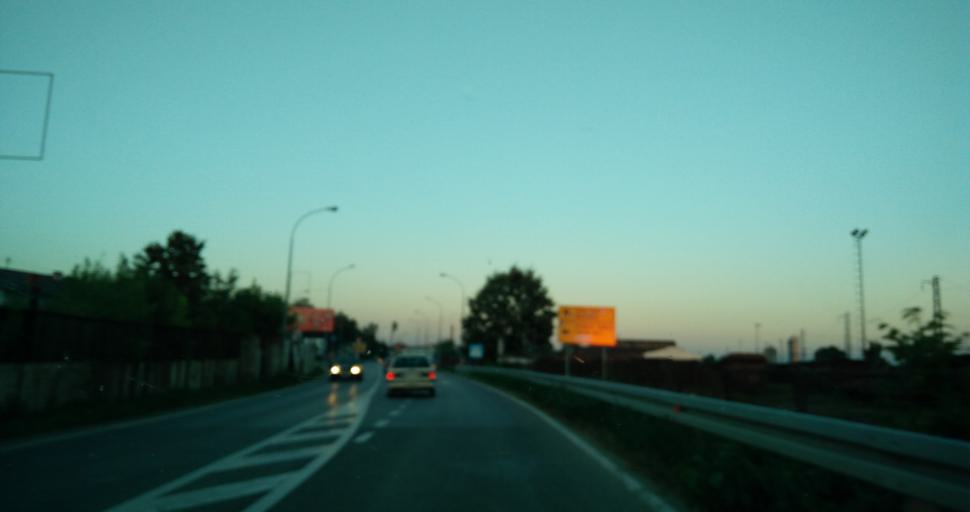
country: BA
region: Republika Srpska
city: Prijedor
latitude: 44.9802
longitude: 16.7158
